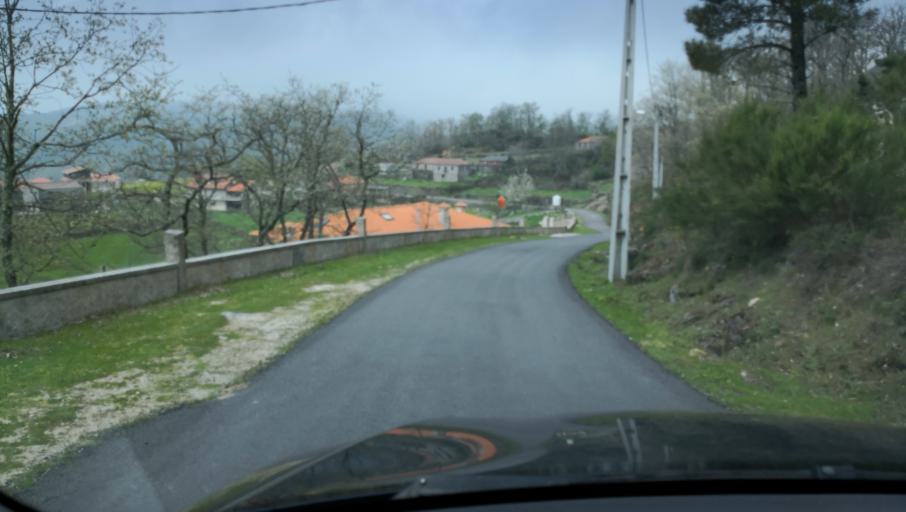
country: PT
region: Vila Real
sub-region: Vila Real
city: Vila Real
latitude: 41.2965
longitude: -7.8289
